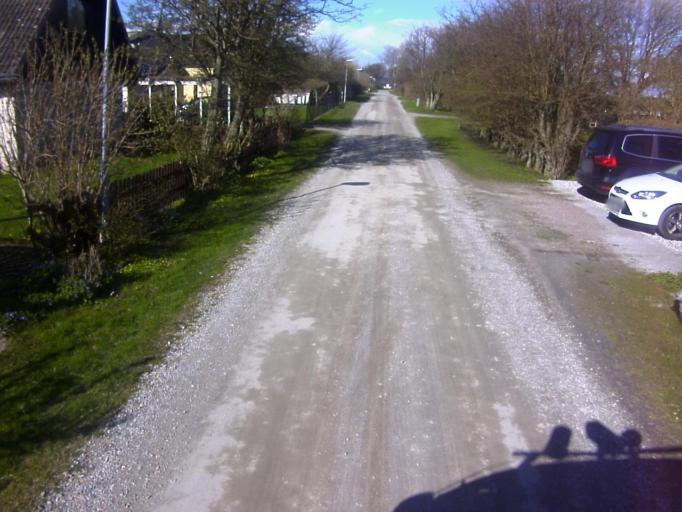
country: SE
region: Skane
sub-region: Kavlinge Kommun
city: Hofterup
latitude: 55.7584
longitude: 12.9084
